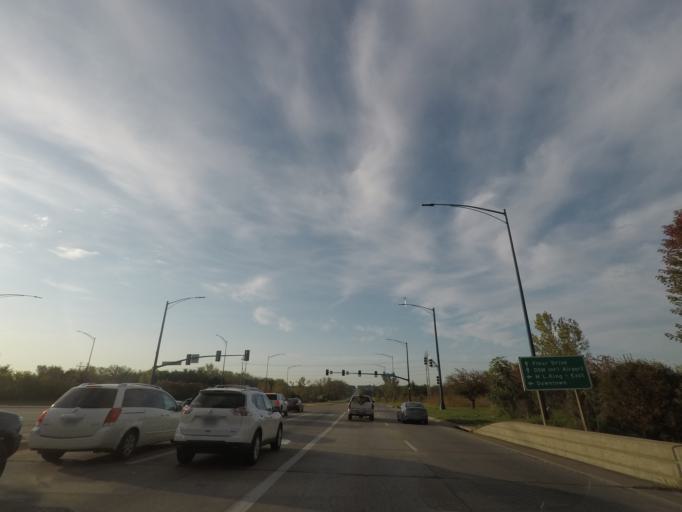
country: US
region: Iowa
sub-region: Polk County
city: Des Moines
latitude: 41.5807
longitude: -93.6449
